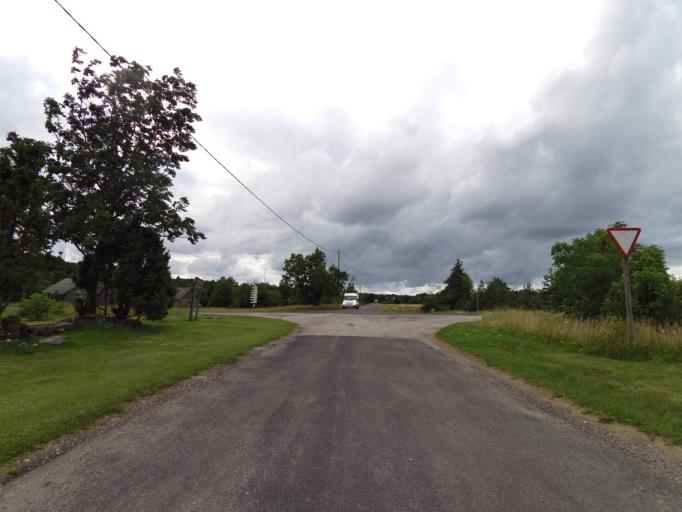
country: EE
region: Laeaene
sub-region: Vormsi vald
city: Hullo
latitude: 58.9876
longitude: 23.2457
